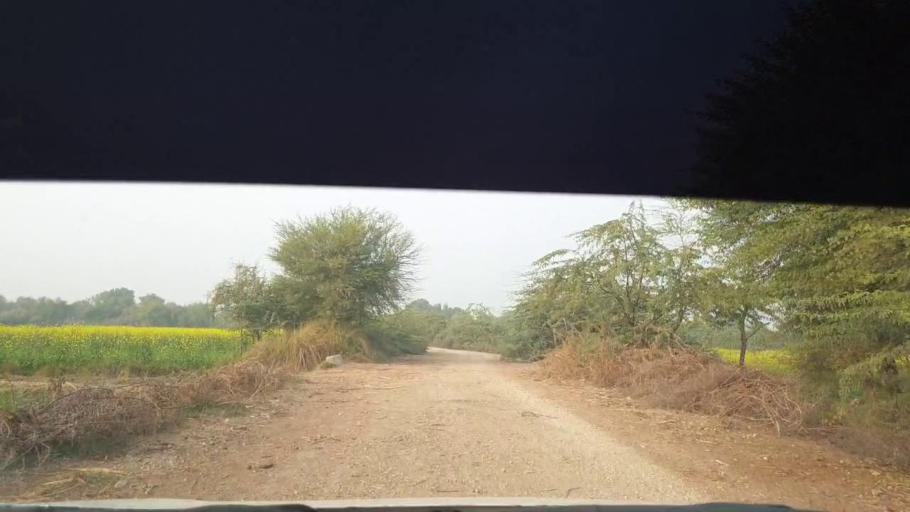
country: PK
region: Sindh
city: Berani
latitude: 25.8301
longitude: 68.8913
